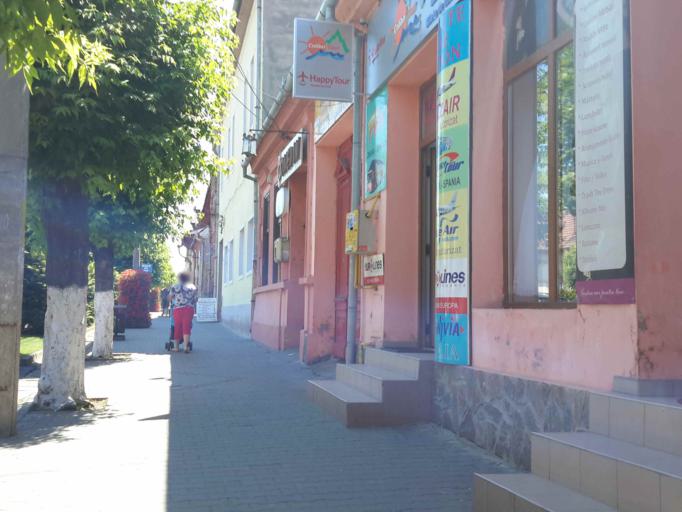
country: RO
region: Alba
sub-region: Municipiul Blaj
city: Blaj
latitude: 46.1767
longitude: 23.9182
